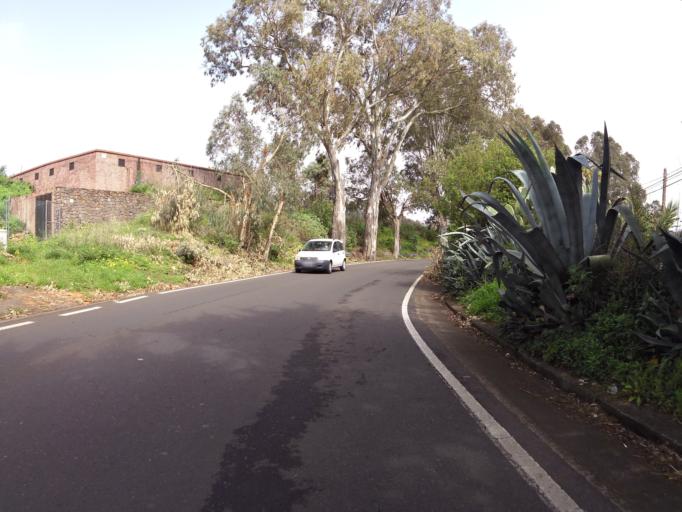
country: ES
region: Canary Islands
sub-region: Provincia de Las Palmas
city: Teror
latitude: 28.0730
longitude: -15.5397
